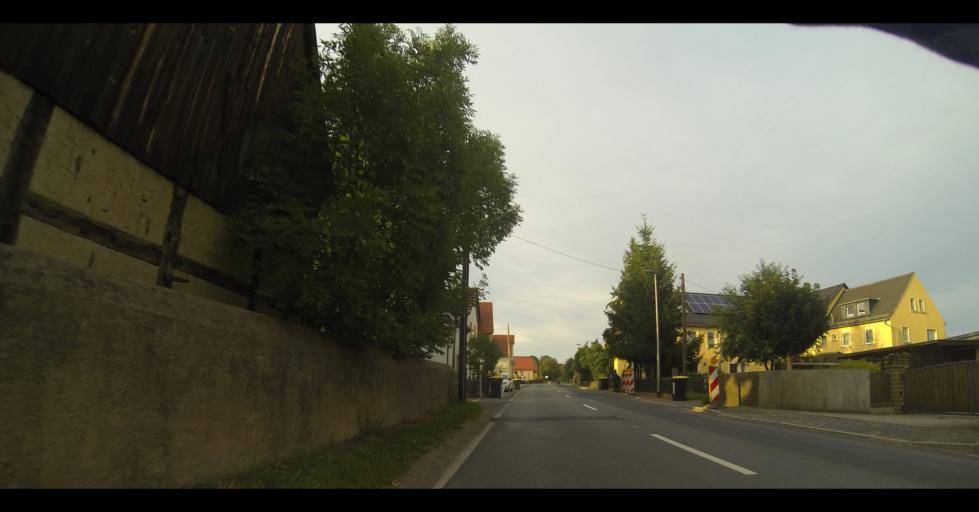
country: DE
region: Saxony
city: Radeburg
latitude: 51.1844
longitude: 13.7219
